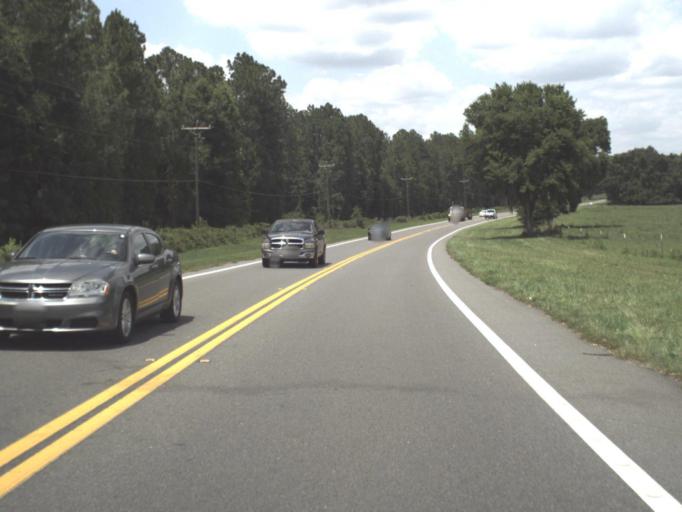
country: US
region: Florida
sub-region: Alachua County
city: Gainesville
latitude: 29.5860
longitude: -82.3916
